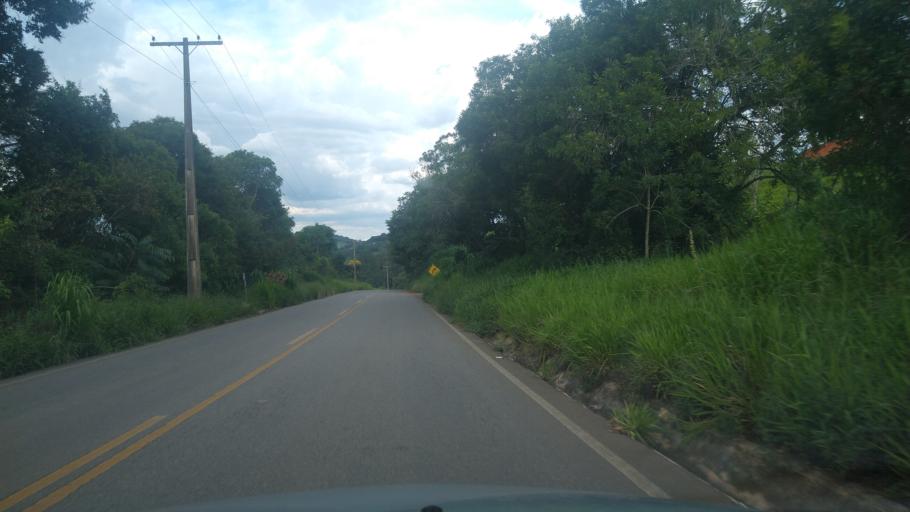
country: BR
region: Minas Gerais
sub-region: Extrema
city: Extrema
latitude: -22.8073
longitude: -46.3067
